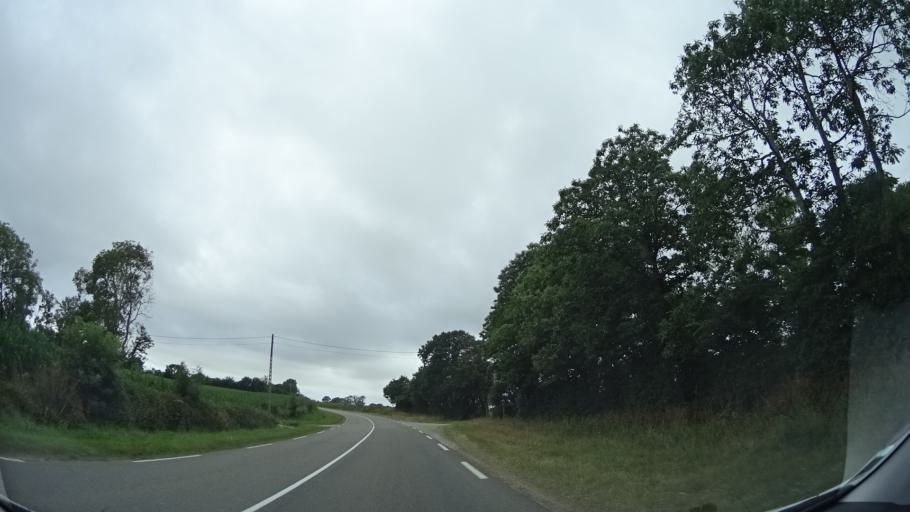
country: FR
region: Lower Normandy
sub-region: Departement de la Manche
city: Portbail
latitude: 49.3189
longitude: -1.6206
